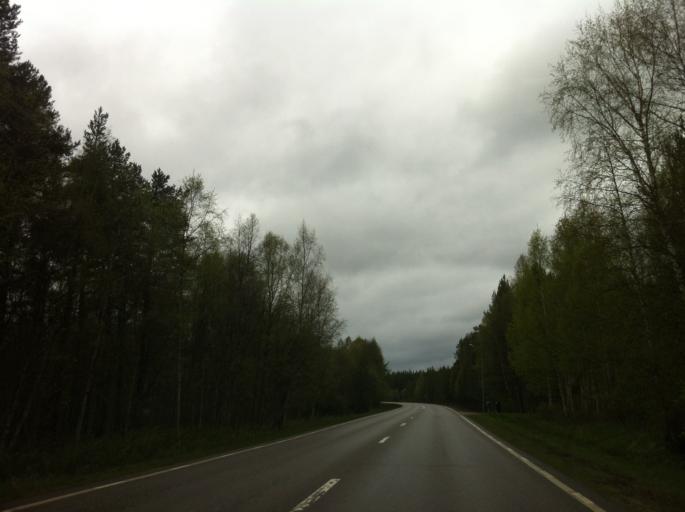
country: SE
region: Jaemtland
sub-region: Harjedalens Kommun
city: Sveg
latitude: 62.1317
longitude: 14.0561
